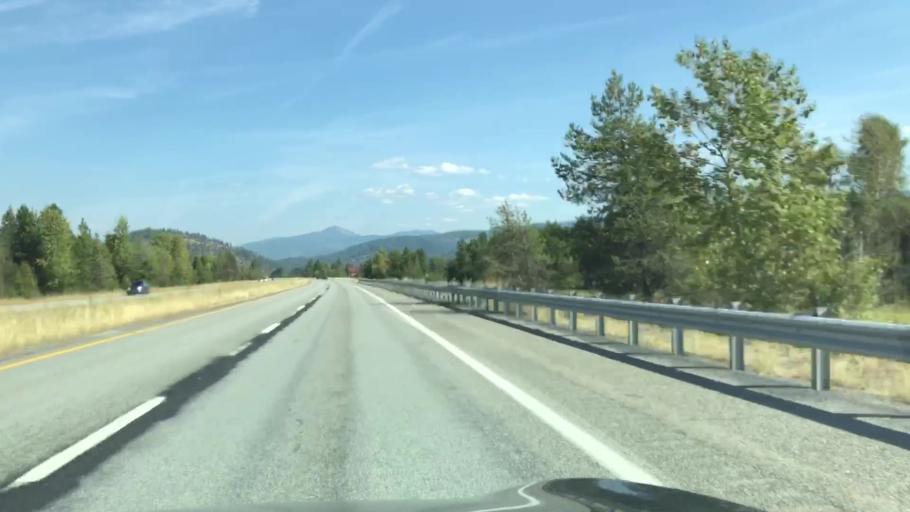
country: US
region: Idaho
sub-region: Shoshone County
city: Pinehurst
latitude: 47.5575
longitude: -116.3864
